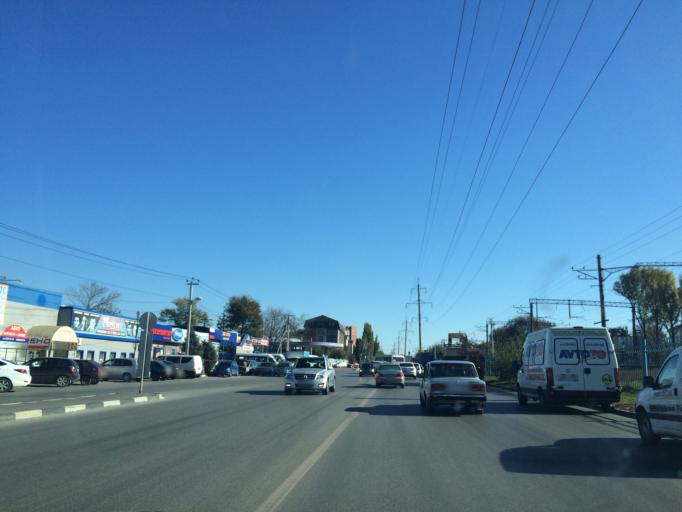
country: RU
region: Rostov
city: Rostov-na-Donu
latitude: 47.2452
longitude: 39.6980
